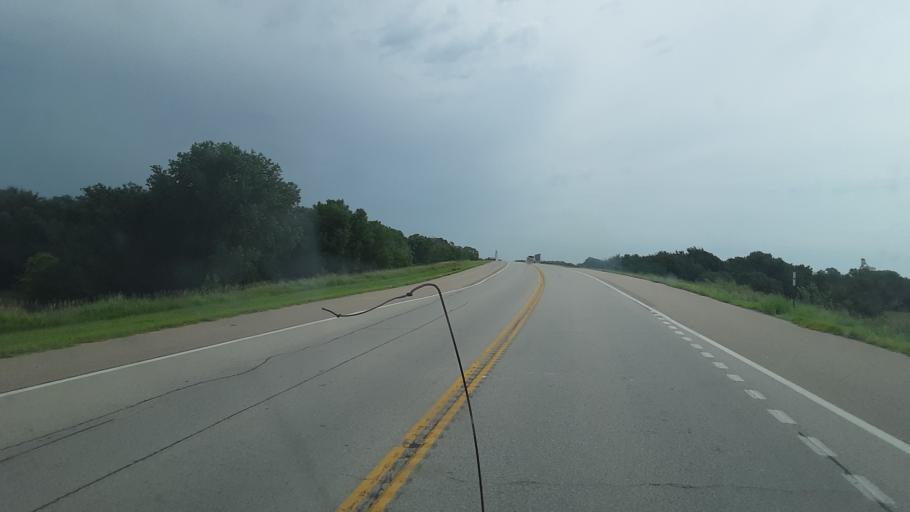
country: US
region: Kansas
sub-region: Stafford County
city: Stafford
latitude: 37.9570
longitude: -98.4212
